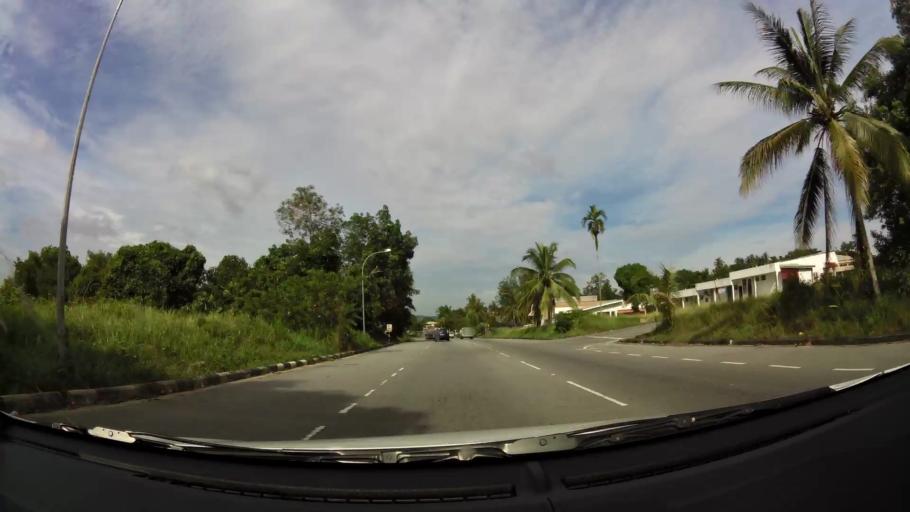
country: BN
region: Brunei and Muara
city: Bandar Seri Begawan
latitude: 4.9014
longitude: 114.8872
